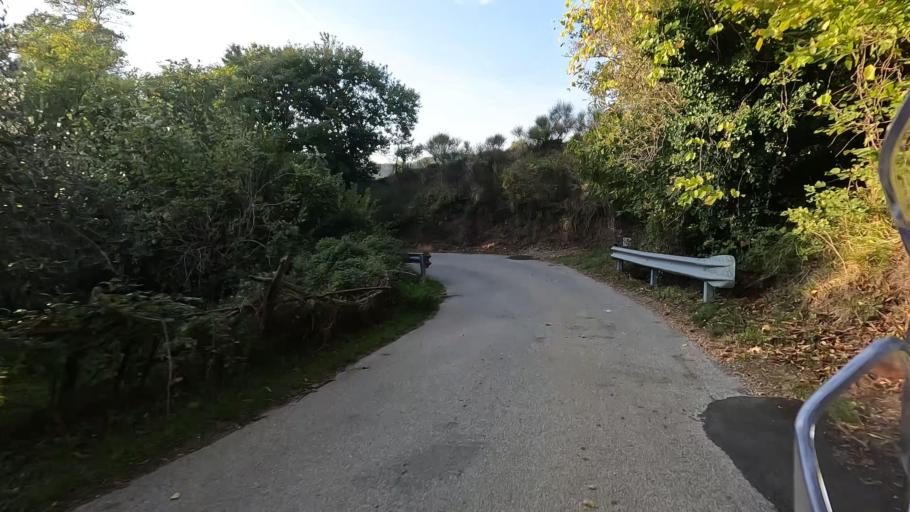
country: IT
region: Liguria
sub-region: Provincia di Savona
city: San Giovanni
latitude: 44.3931
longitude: 8.5295
